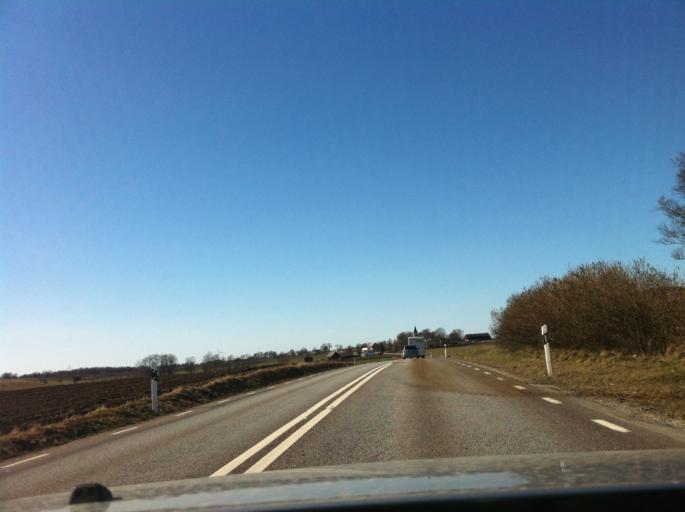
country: SE
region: Joenkoeping
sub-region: Mullsjo Kommun
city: Mullsjoe
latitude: 58.0769
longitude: 13.7922
